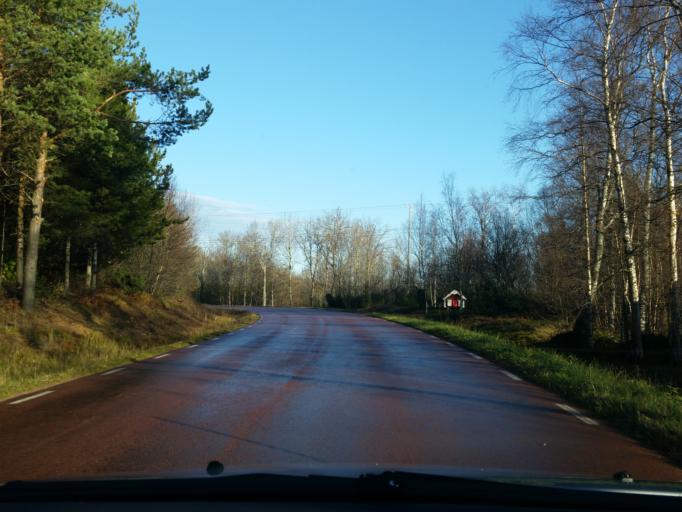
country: AX
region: Alands skaergard
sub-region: Braendoe
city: Braendoe
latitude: 60.4207
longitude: 21.0483
